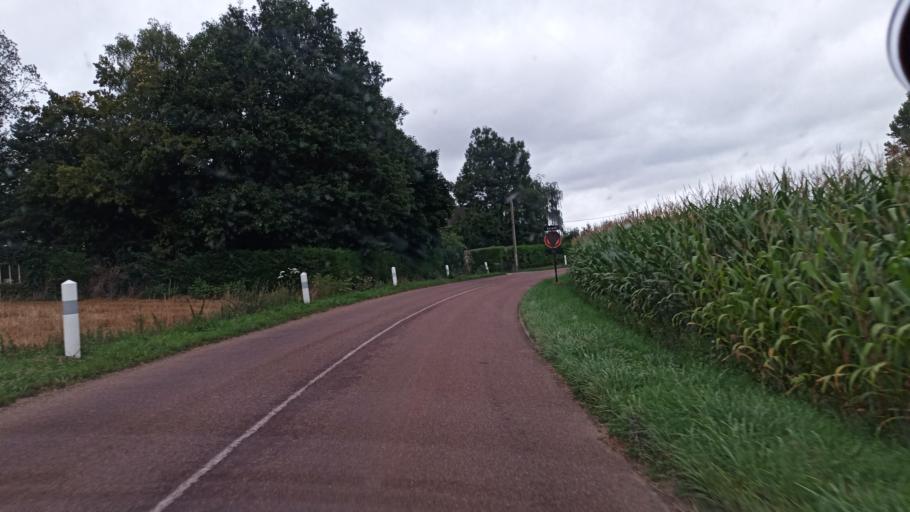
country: FR
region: Ile-de-France
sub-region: Departement de Seine-et-Marne
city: Voulx
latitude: 48.2683
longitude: 3.0010
